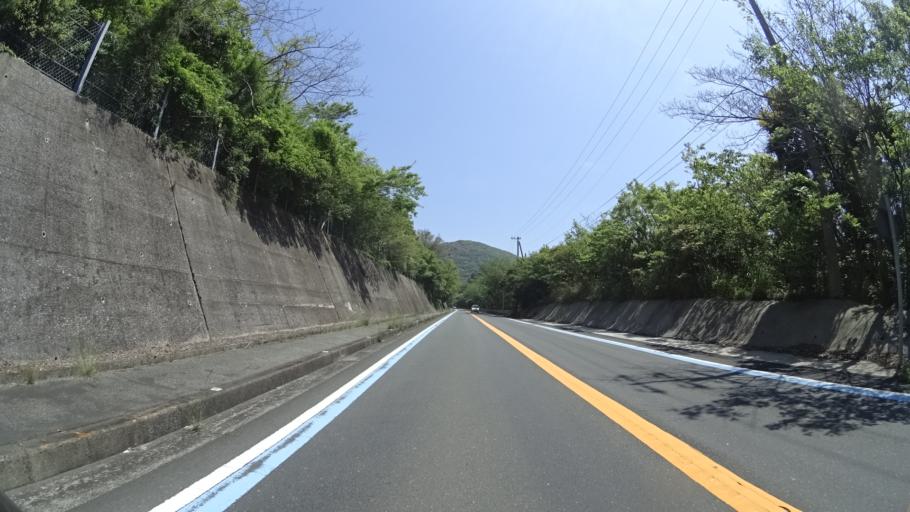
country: JP
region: Ehime
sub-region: Nishiuwa-gun
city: Ikata-cho
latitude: 33.4484
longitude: 132.2678
